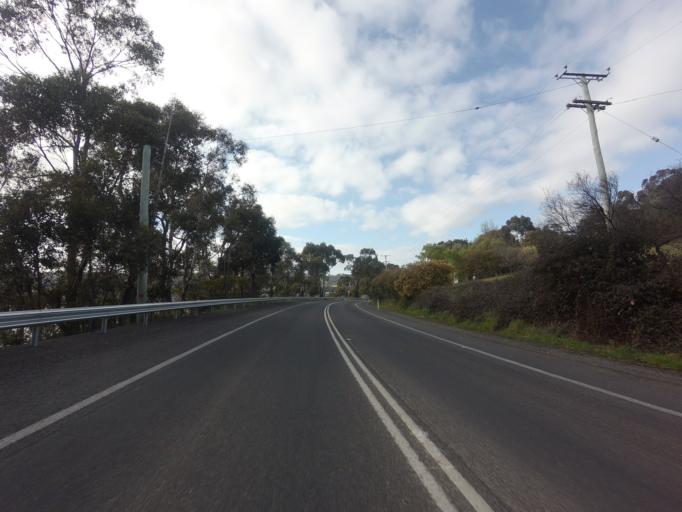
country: AU
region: Tasmania
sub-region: Huon Valley
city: Geeveston
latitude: -43.1493
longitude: 146.9794
